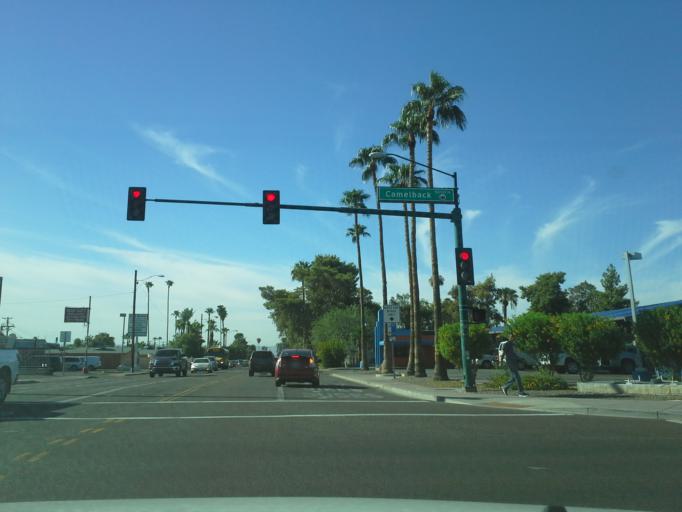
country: US
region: Arizona
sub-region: Maricopa County
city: Phoenix
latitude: 33.5095
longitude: -112.0913
